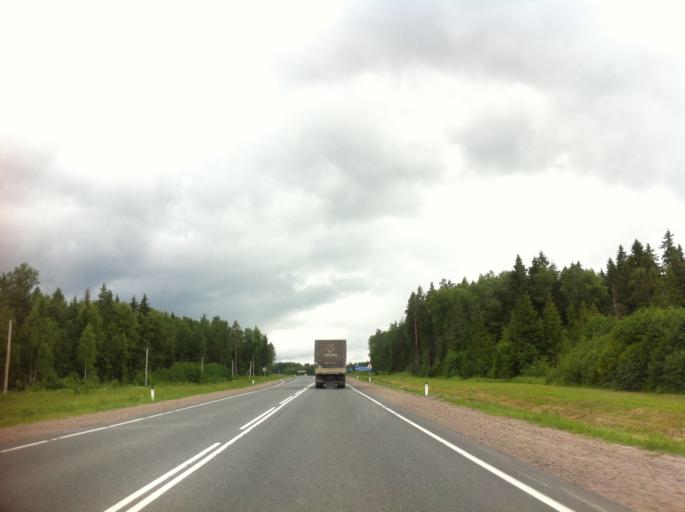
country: RU
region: Leningrad
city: Luga
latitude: 58.6614
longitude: 29.8630
